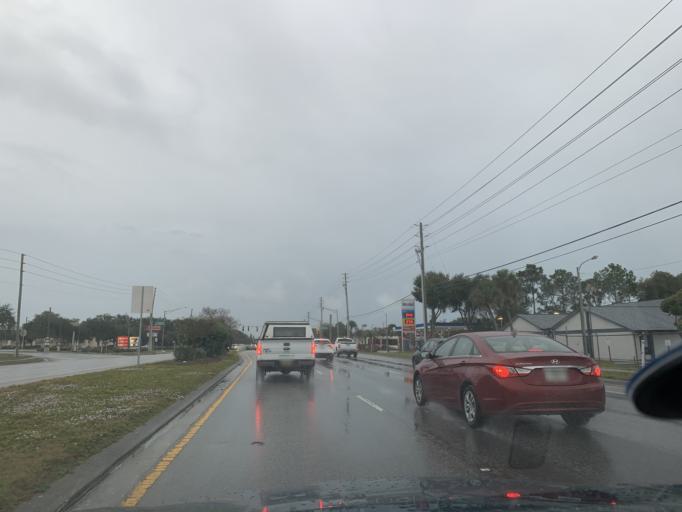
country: US
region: Florida
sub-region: Pasco County
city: Jasmine Estates
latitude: 28.2931
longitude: -82.6759
